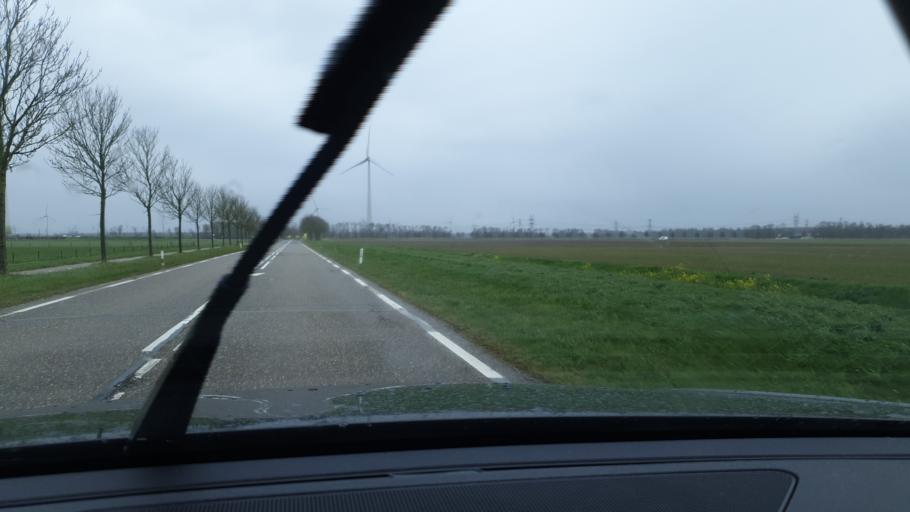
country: NL
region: Flevoland
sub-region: Gemeente Lelystad
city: Lelystad
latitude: 52.5540
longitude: 5.5711
